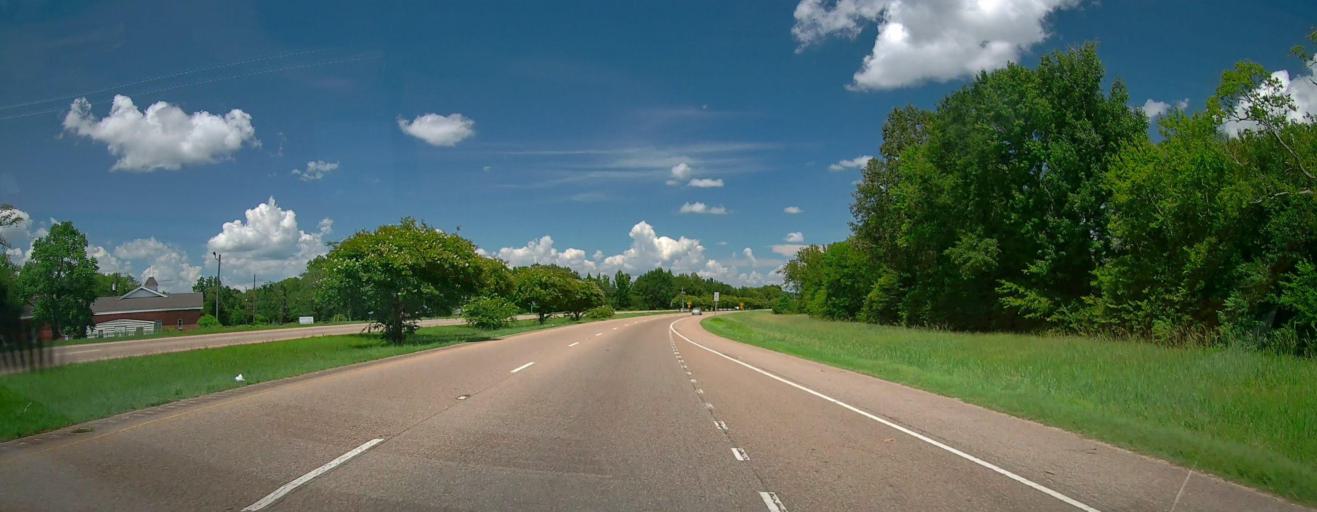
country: US
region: Alabama
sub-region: Montgomery County
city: Montgomery
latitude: 32.4069
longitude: -86.3075
